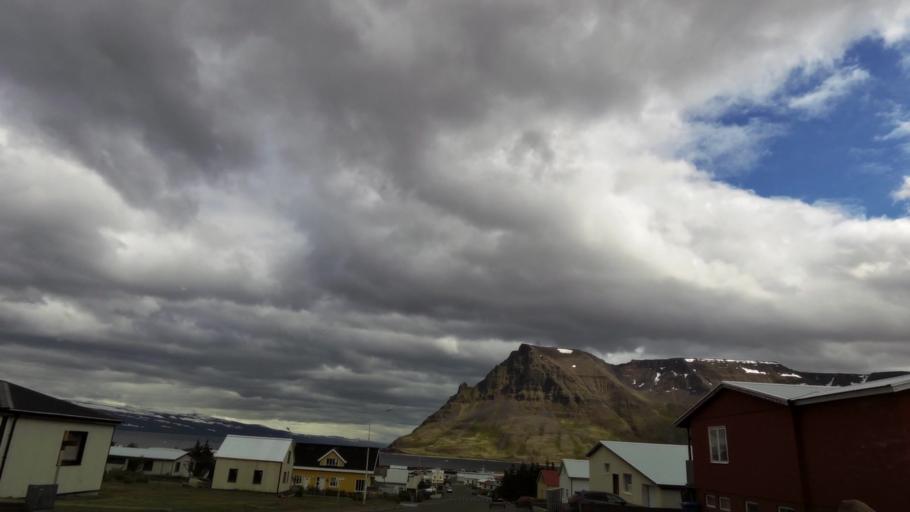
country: IS
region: Westfjords
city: Isafjoerdur
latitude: 66.1582
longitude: -23.2591
